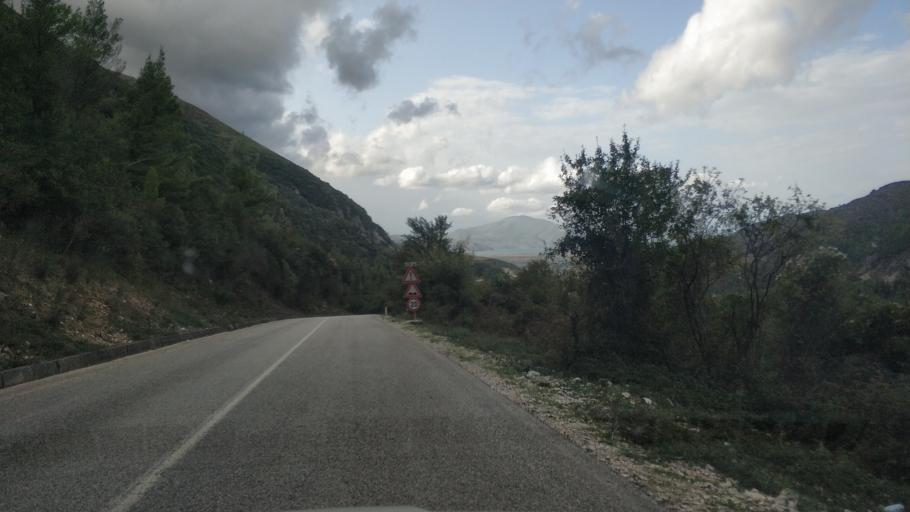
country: AL
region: Vlore
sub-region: Rrethi i Vlores
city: Orikum
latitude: 40.2545
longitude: 19.5333
